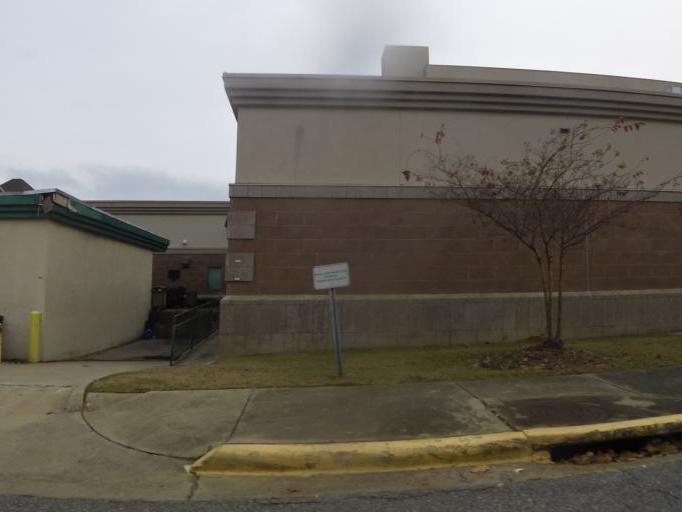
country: US
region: Alabama
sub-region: Montgomery County
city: Montgomery
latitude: 32.3795
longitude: -86.3147
